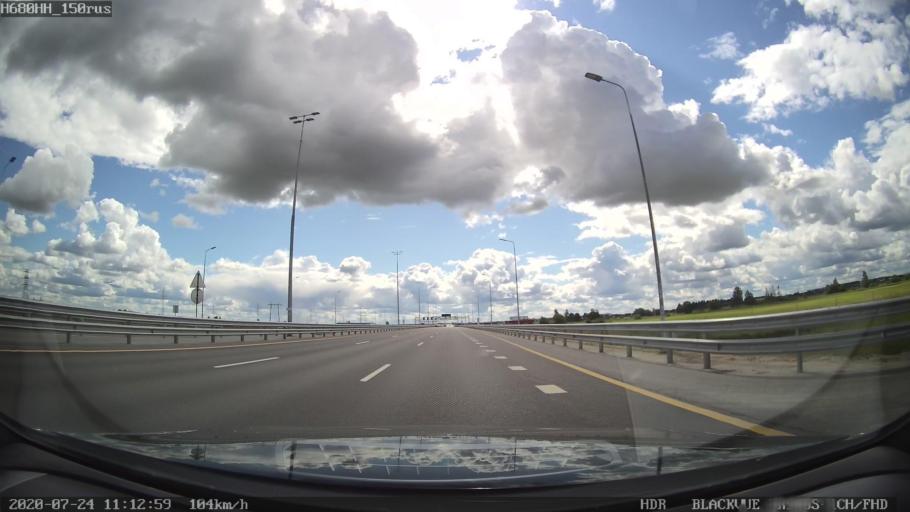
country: RU
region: Leningrad
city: Fedorovskoye
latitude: 59.7049
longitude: 30.5465
